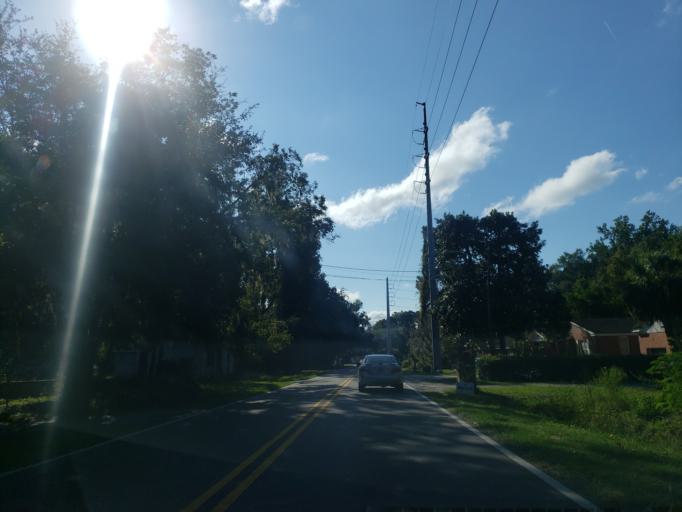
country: US
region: Georgia
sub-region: Chatham County
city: Isle of Hope
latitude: 31.9919
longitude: -81.0774
